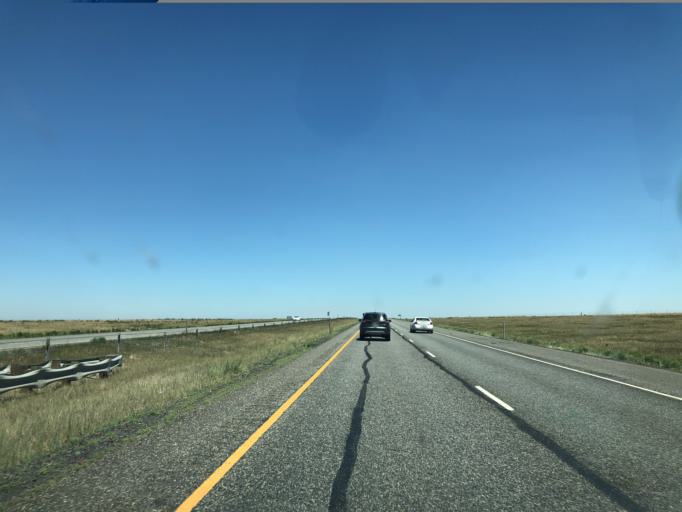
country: US
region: Colorado
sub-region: Adams County
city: Aurora
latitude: 39.7851
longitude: -104.7162
